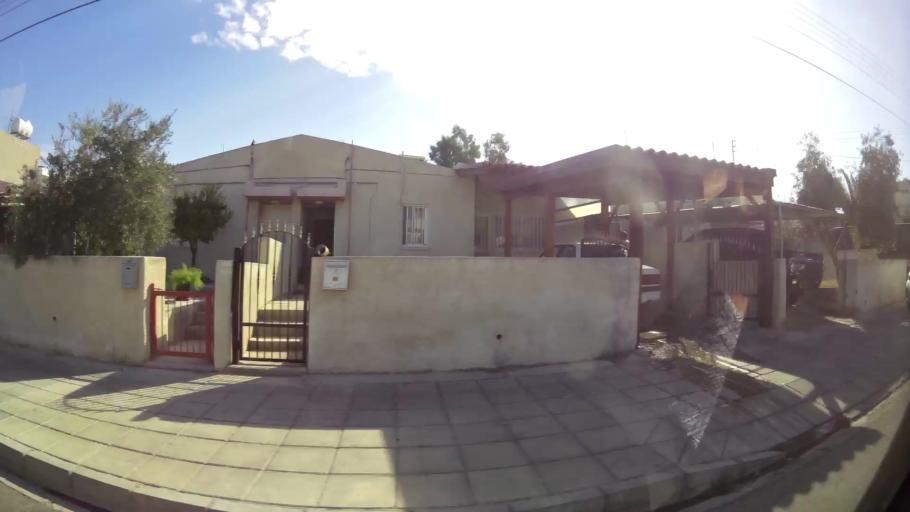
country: CY
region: Lefkosia
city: Nicosia
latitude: 35.1286
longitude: 33.3471
